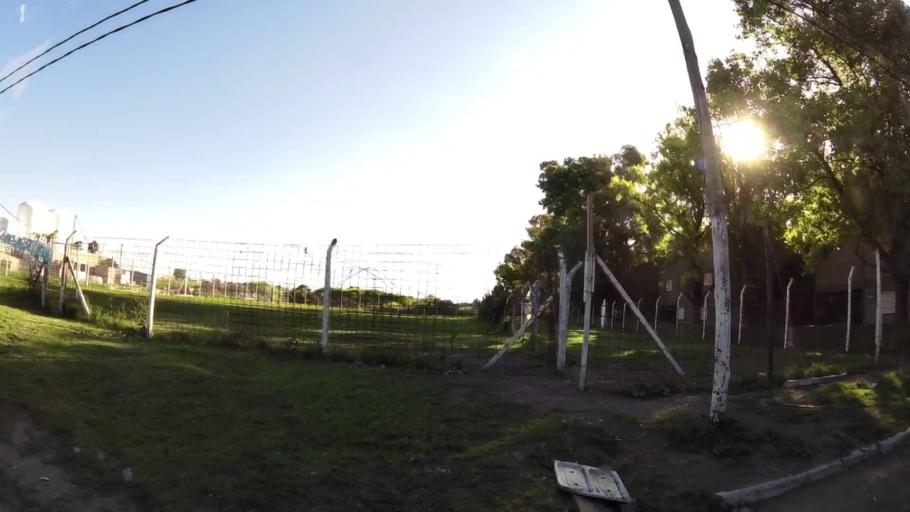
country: AR
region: Buenos Aires
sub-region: Partido de Moron
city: Moron
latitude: -34.6880
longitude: -58.6272
